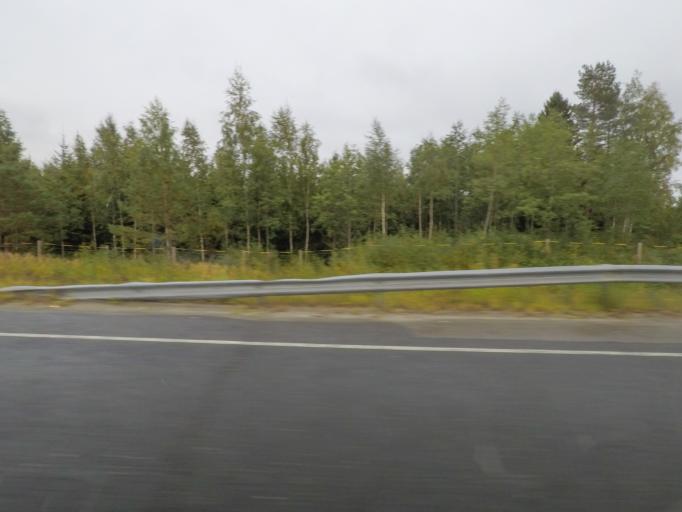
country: FI
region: Northern Savo
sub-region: Kuopio
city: Kuopio
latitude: 62.6968
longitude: 27.5676
